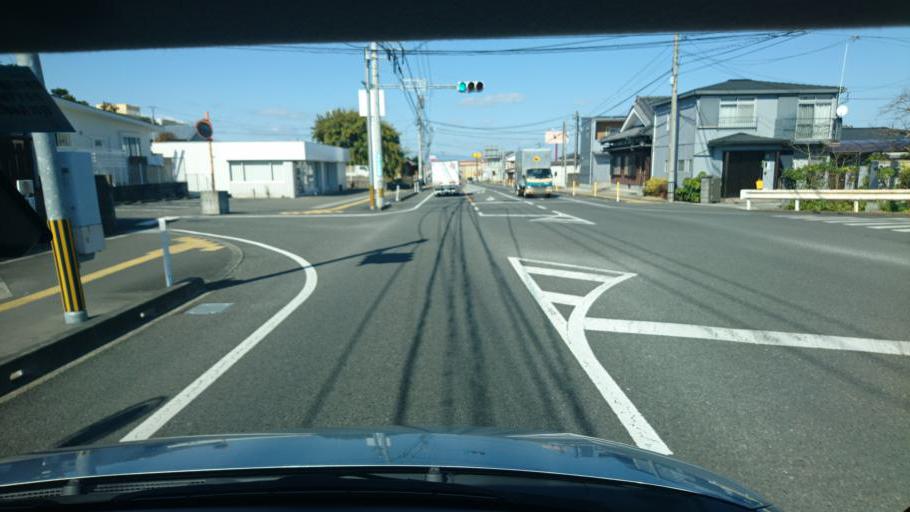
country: JP
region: Miyazaki
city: Miyazaki-shi
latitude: 31.8694
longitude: 131.4316
